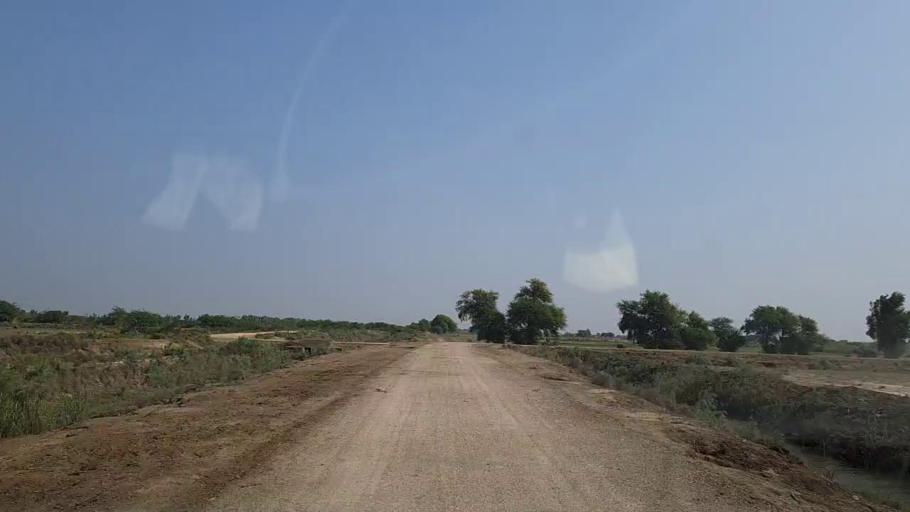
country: PK
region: Sindh
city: Mirpur Sakro
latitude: 24.5319
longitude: 67.7886
